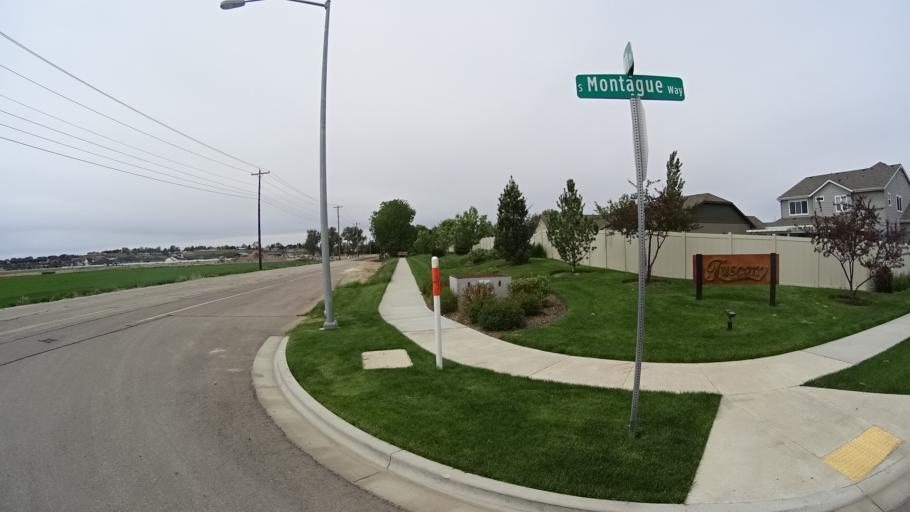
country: US
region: Idaho
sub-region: Ada County
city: Meridian
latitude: 43.5615
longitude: -116.3595
